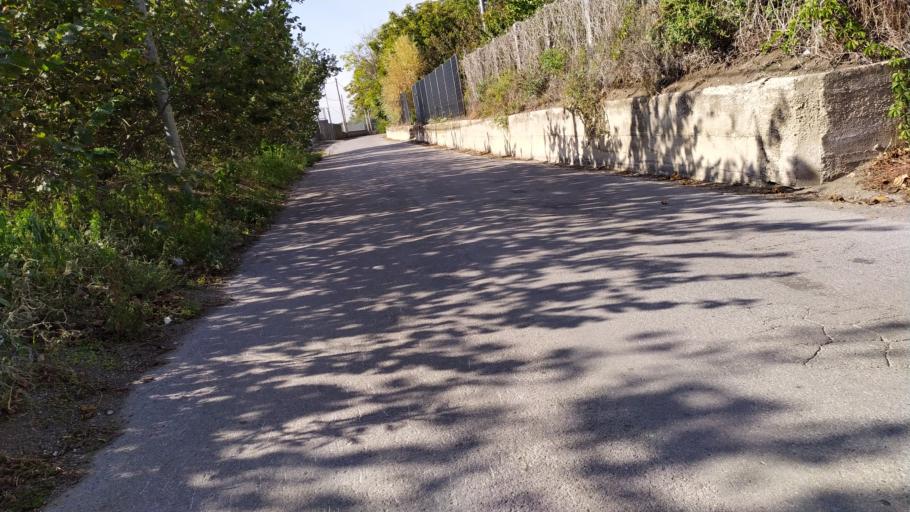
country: IT
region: Campania
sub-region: Provincia di Napoli
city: Striano
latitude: 40.8334
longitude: 14.5869
